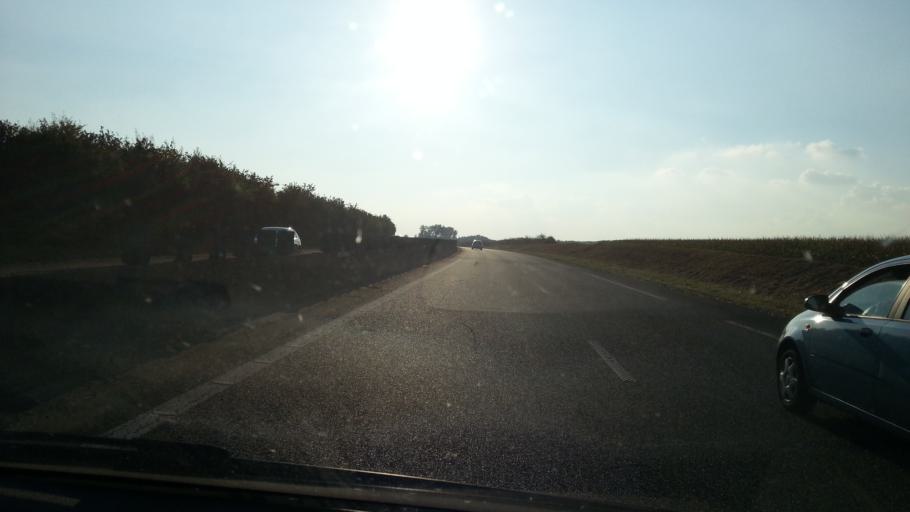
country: FR
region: Picardie
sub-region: Departement de l'Oise
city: Coudun
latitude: 49.4741
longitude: 2.8370
